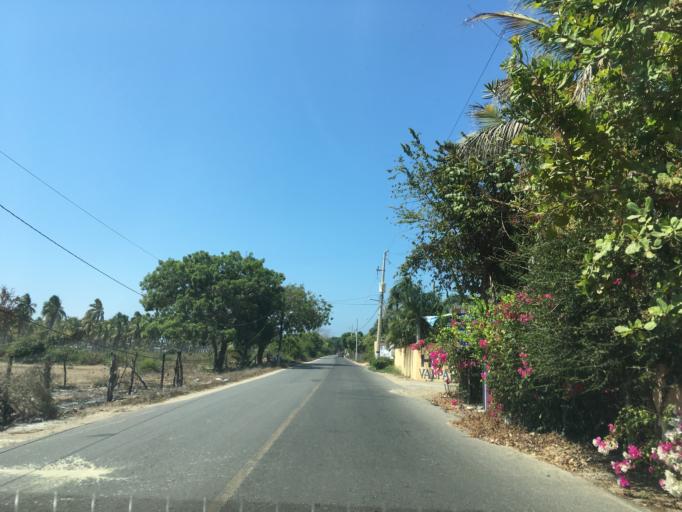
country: MX
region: Guerrero
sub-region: Zihuatanejo de Azueta
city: Los Achotes
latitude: 17.5422
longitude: -101.4396
